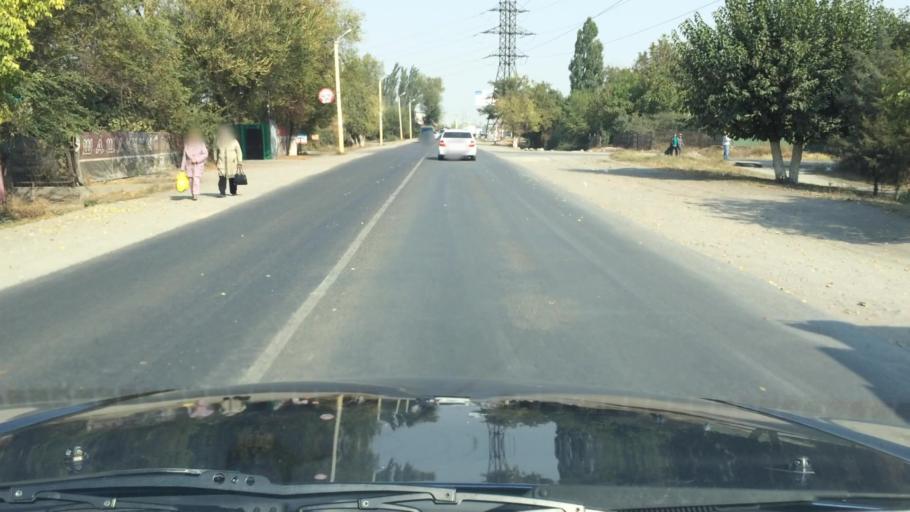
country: KG
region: Chuy
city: Lebedinovka
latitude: 42.8871
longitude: 74.6788
